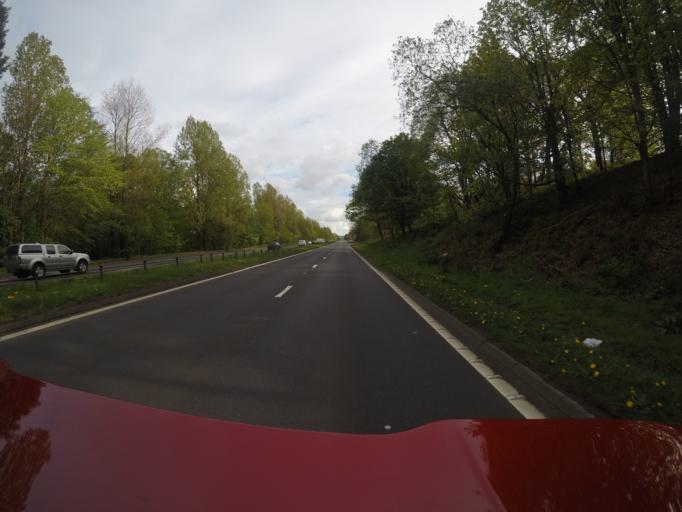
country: GB
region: Scotland
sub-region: West Dunbartonshire
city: Renton
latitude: 55.9784
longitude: -4.5878
